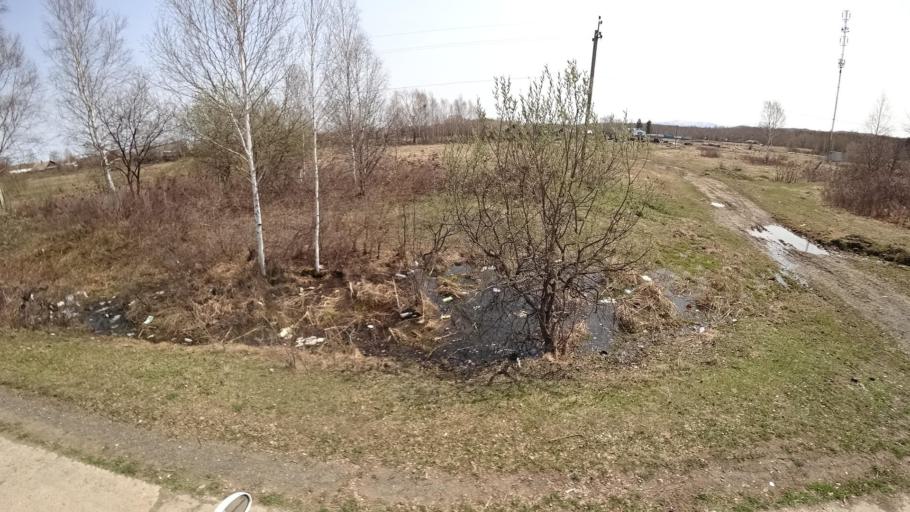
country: RU
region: Khabarovsk Krai
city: Selikhino
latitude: 50.3858
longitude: 137.3734
